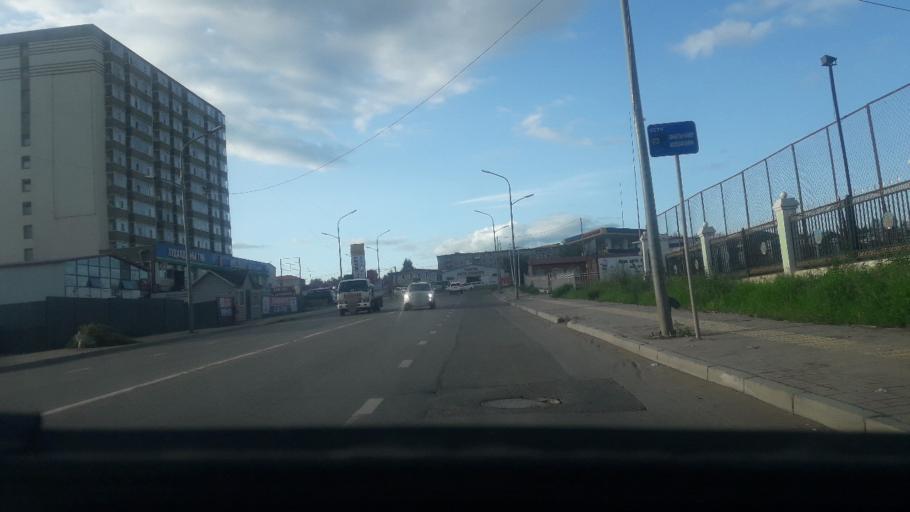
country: MN
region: Ulaanbaatar
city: Ulaanbaatar
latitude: 47.9222
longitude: 106.9858
